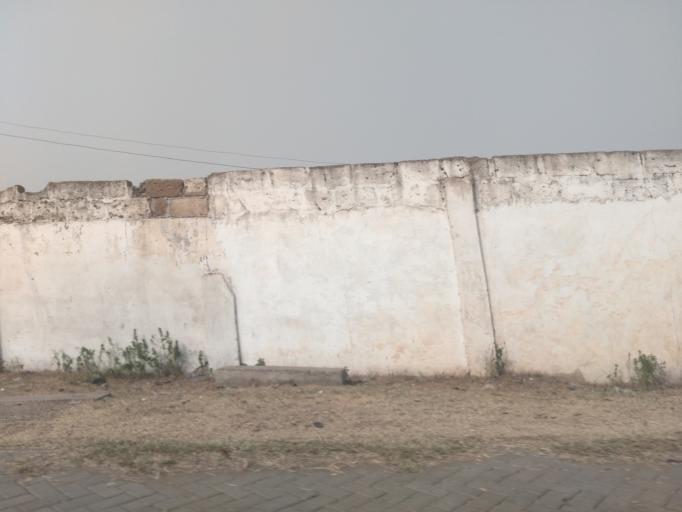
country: GH
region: Greater Accra
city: Accra
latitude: 5.5357
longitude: -0.2164
